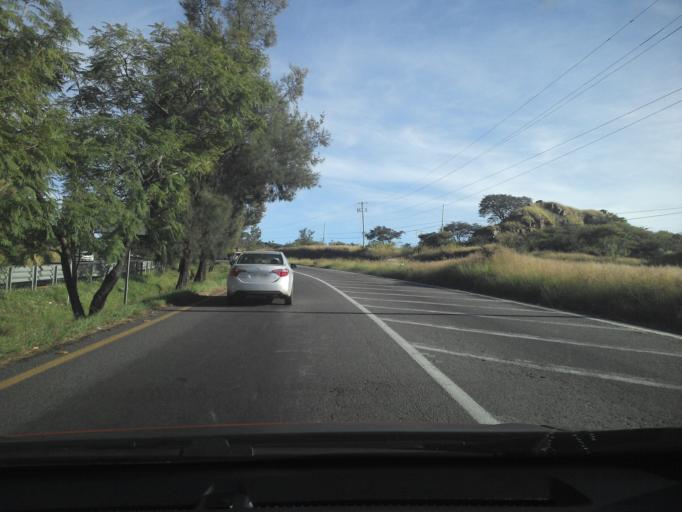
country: MX
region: Jalisco
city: La Venta del Astillero
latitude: 20.7329
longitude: -103.5774
